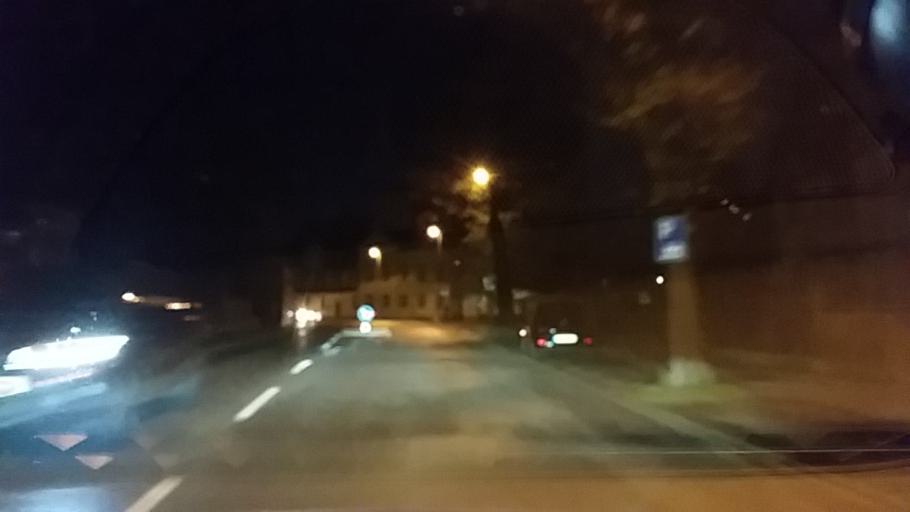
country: DE
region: Lower Saxony
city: Braunschweig
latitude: 52.2886
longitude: 10.4946
